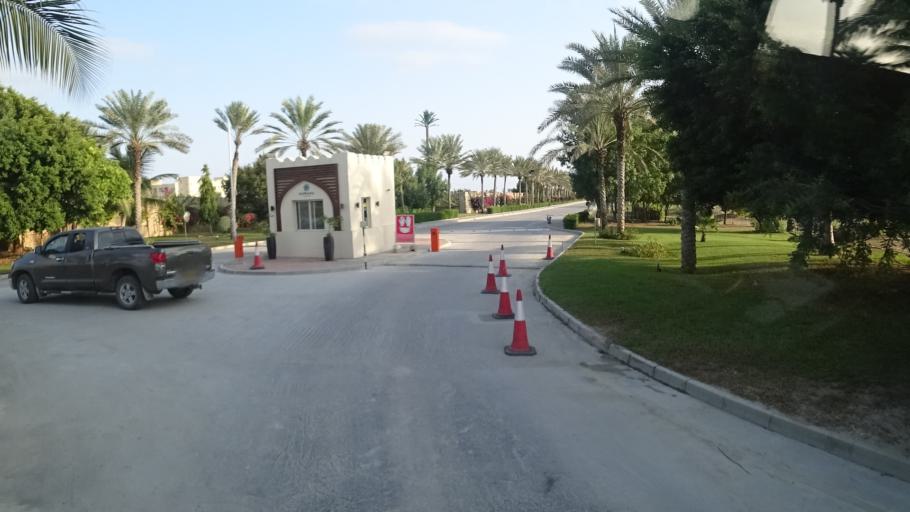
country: OM
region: Zufar
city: Salalah
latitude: 17.0386
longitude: 54.3032
